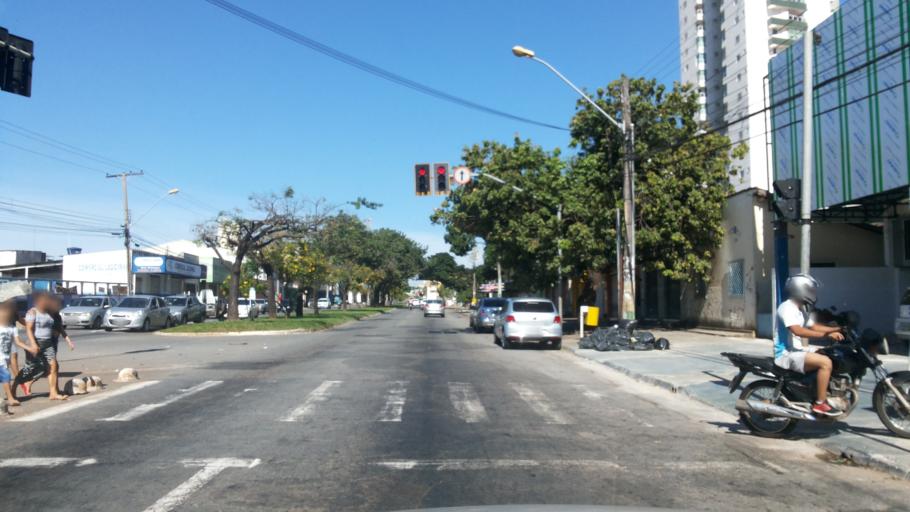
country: BR
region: Goias
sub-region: Goiania
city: Goiania
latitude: -16.7178
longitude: -49.2567
